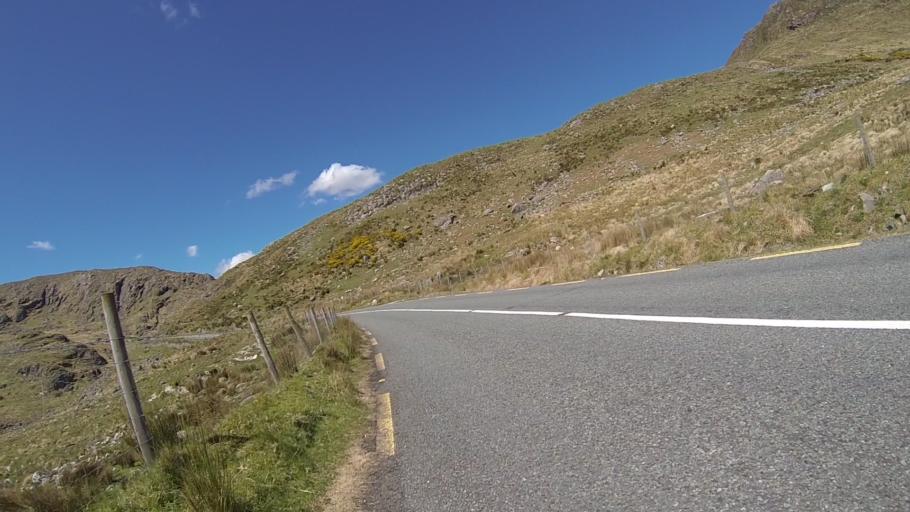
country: IE
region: Munster
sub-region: Ciarrai
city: Kenmare
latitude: 51.9325
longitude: -9.6497
